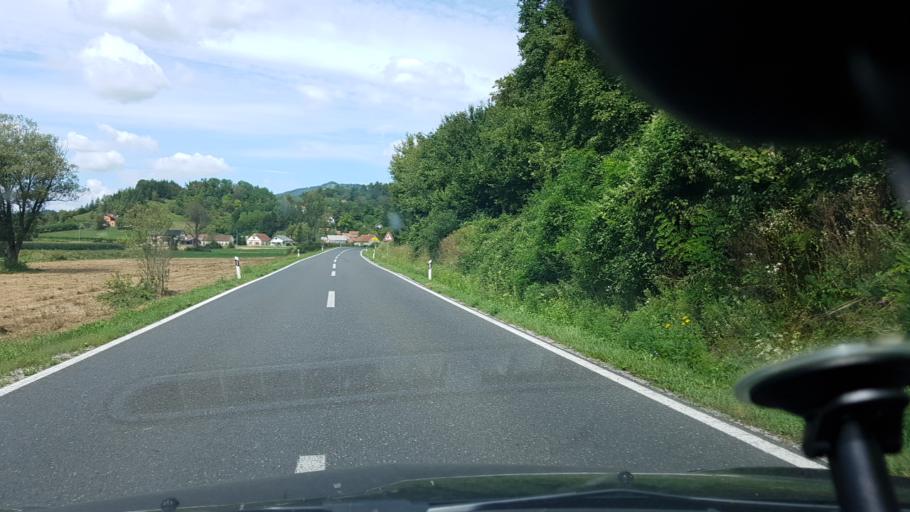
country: HR
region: Varazdinska
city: Lepoglava
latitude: 46.2257
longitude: 15.9933
